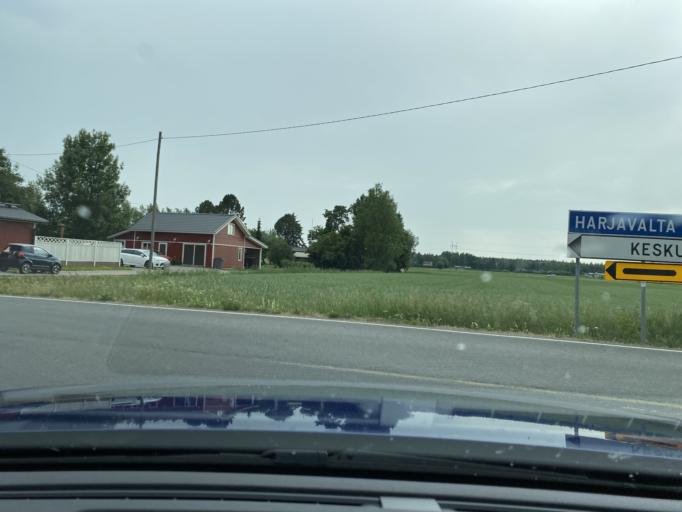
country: FI
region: Satakunta
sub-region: Rauma
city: Eura
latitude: 61.1421
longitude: 22.1189
